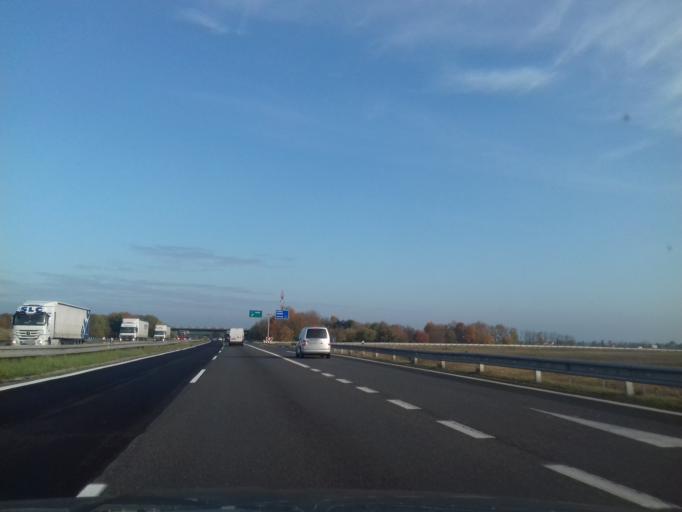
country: SK
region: Bratislavsky
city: Stupava
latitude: 48.3233
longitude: 17.0233
